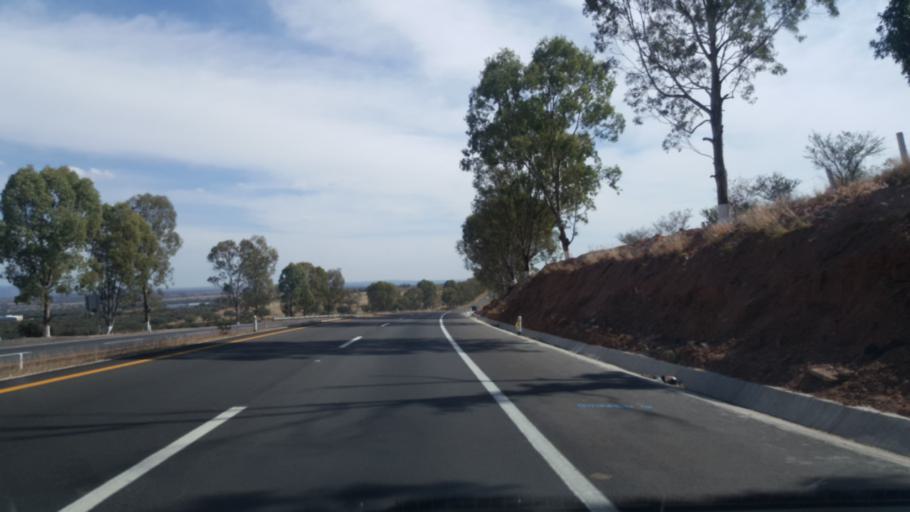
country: MX
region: Jalisco
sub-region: Lagos de Moreno
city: Cristeros [Fraccionamiento]
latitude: 21.2631
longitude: -101.9595
